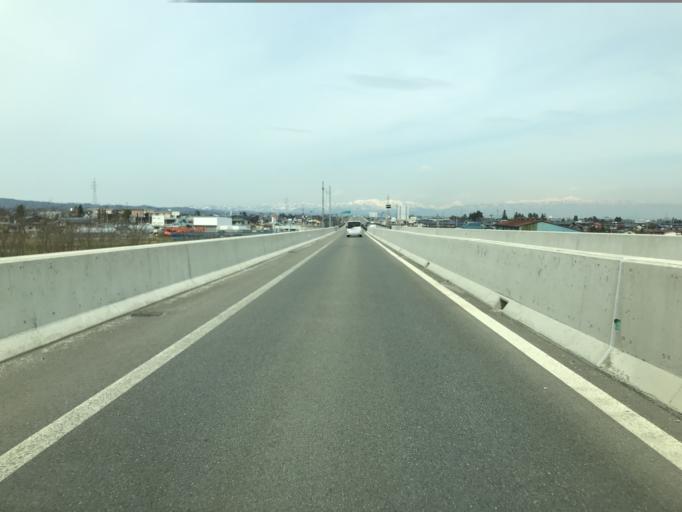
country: JP
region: Yamagata
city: Yonezawa
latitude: 37.9368
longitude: 140.1286
